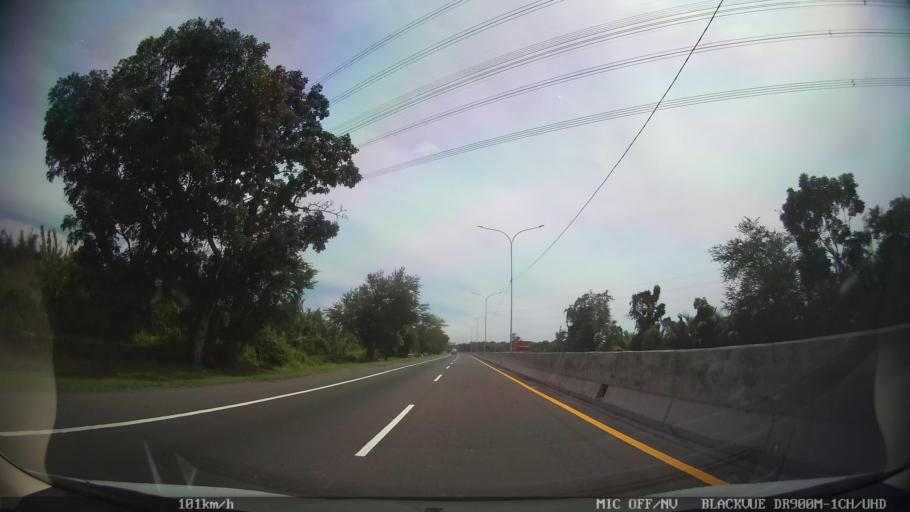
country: ID
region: North Sumatra
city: Labuhan Deli
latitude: 3.7471
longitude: 98.6804
